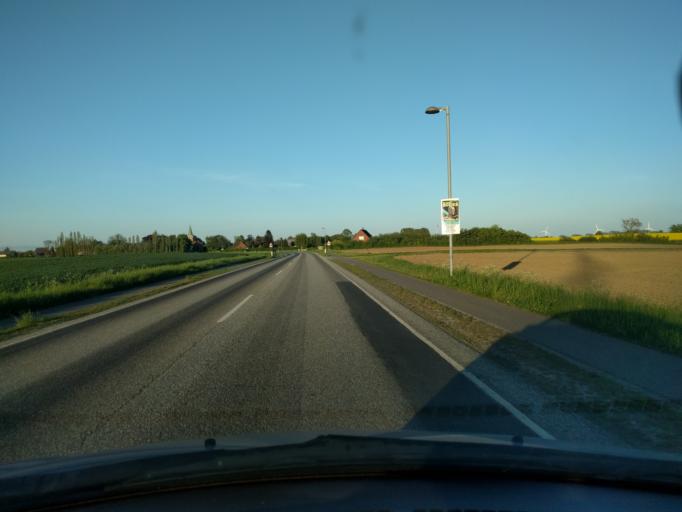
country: DK
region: Zealand
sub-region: Guldborgsund Kommune
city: Nykobing Falster
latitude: 54.7846
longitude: 11.9181
